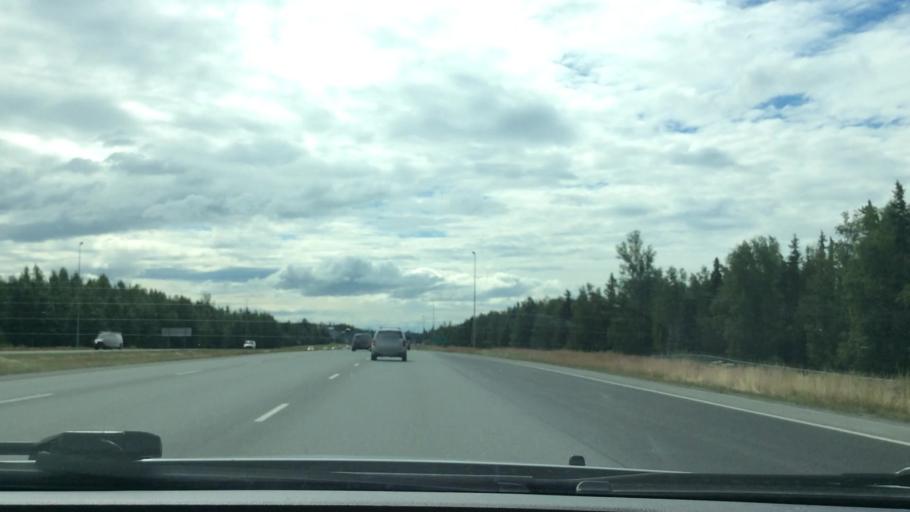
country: US
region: Alaska
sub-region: Anchorage Municipality
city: Elmendorf Air Force Base
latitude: 61.2378
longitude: -149.6959
